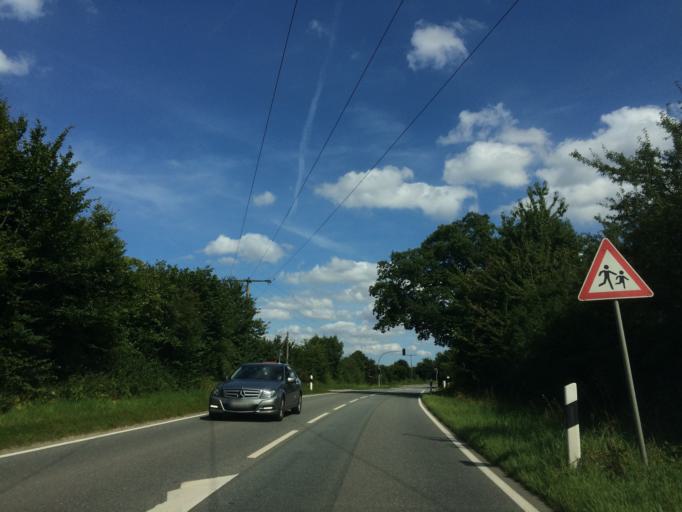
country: DE
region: Schleswig-Holstein
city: Bosdorf
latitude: 54.1476
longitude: 10.4893
